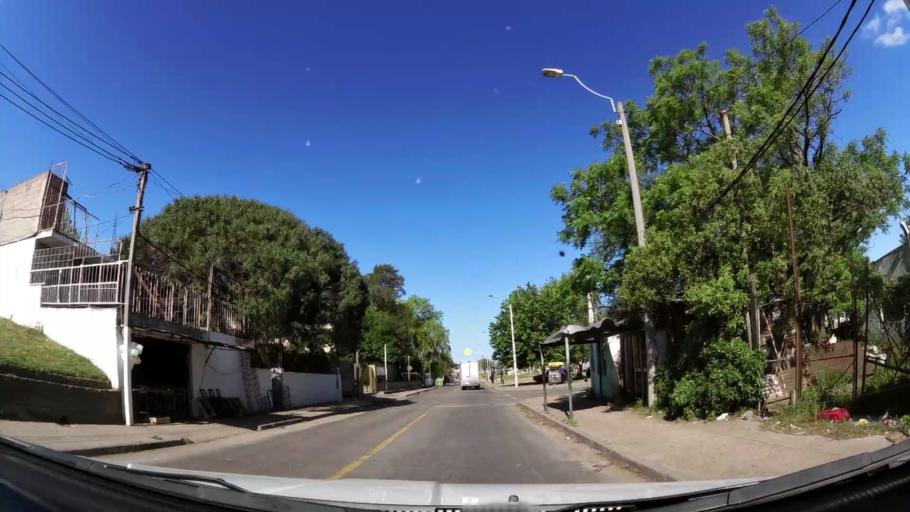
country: UY
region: Montevideo
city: Montevideo
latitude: -34.8350
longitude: -56.1626
